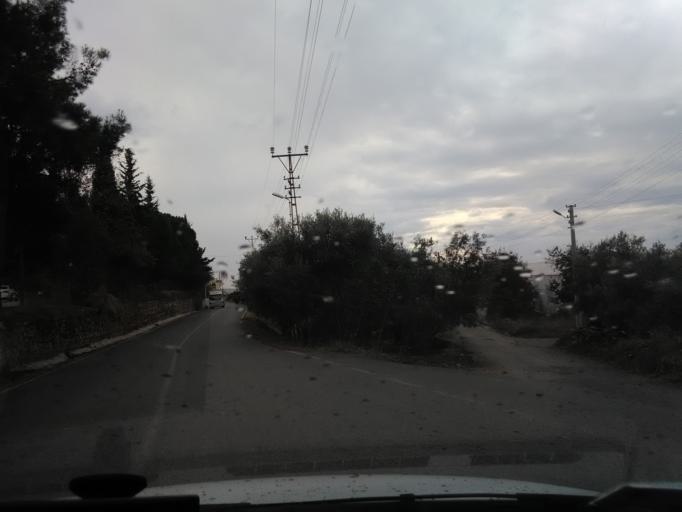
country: TR
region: Antalya
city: Gazipasa
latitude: 36.2583
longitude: 32.3063
